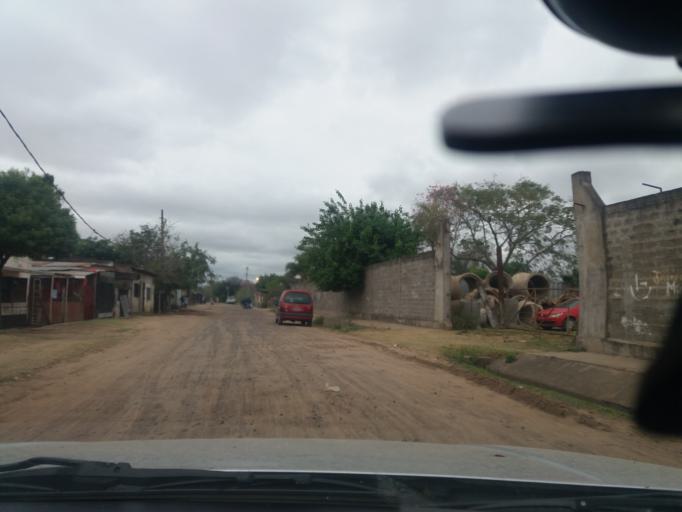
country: AR
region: Corrientes
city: Corrientes
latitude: -27.5121
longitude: -58.8297
